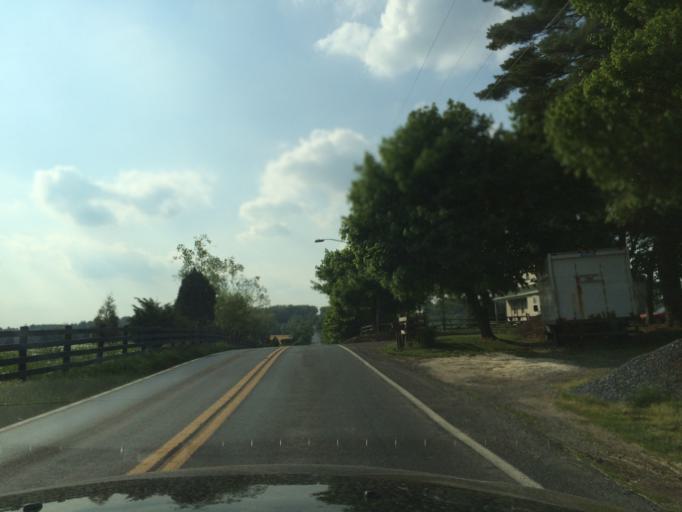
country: US
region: Maryland
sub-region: Carroll County
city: Mount Airy
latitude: 39.3059
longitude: -77.1027
